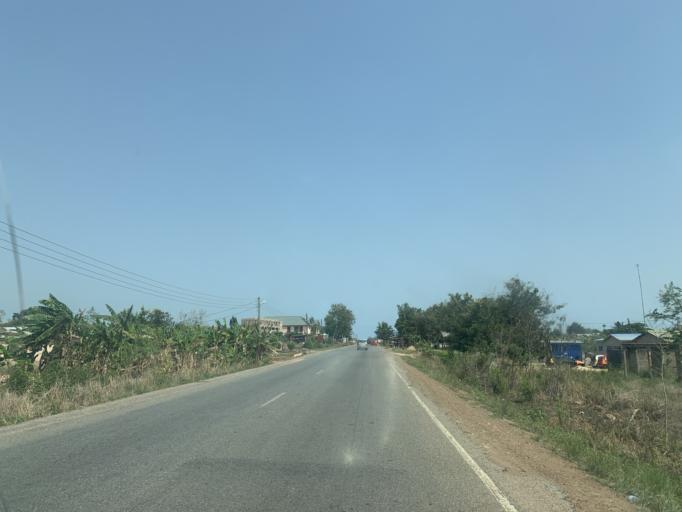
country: GH
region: Central
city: Winneba
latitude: 5.4004
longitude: -0.6508
